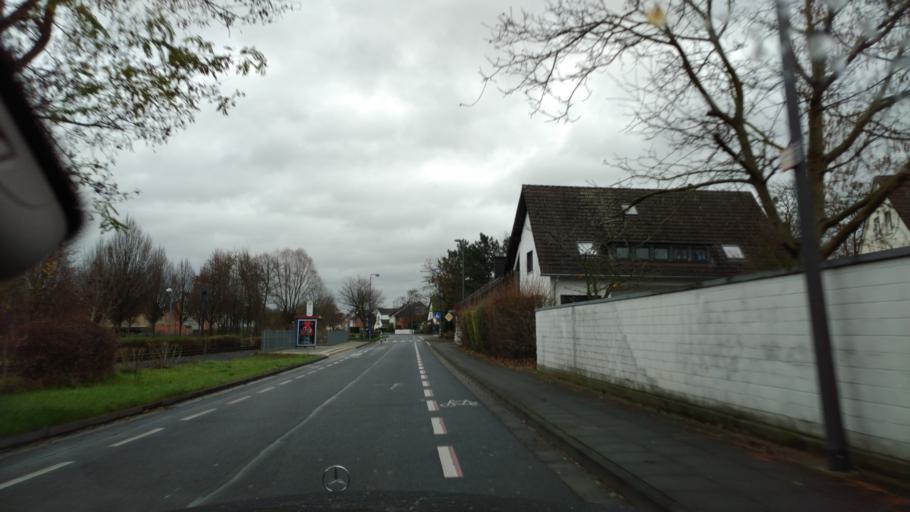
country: DE
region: North Rhine-Westphalia
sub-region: Regierungsbezirk Koln
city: Bonn
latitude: 50.7767
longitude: 7.0957
